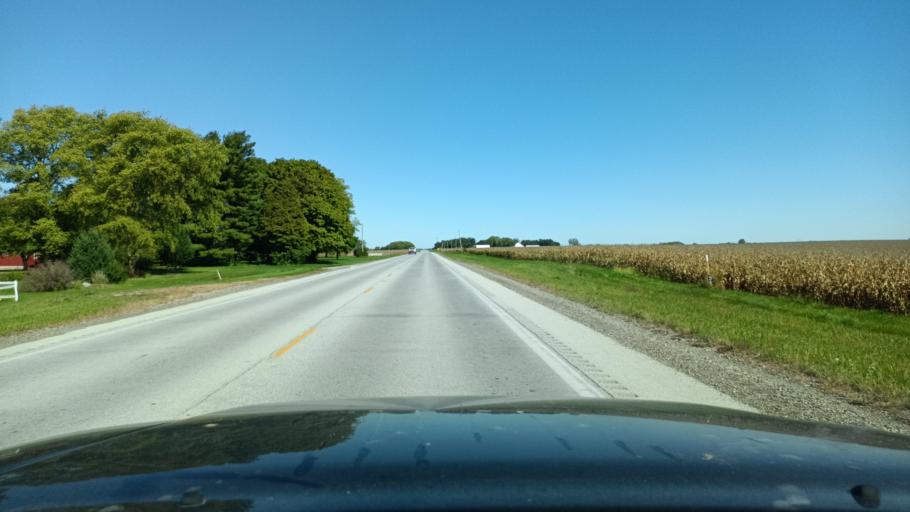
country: US
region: Illinois
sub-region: Champaign County
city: Philo
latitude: 40.0630
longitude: -88.1618
